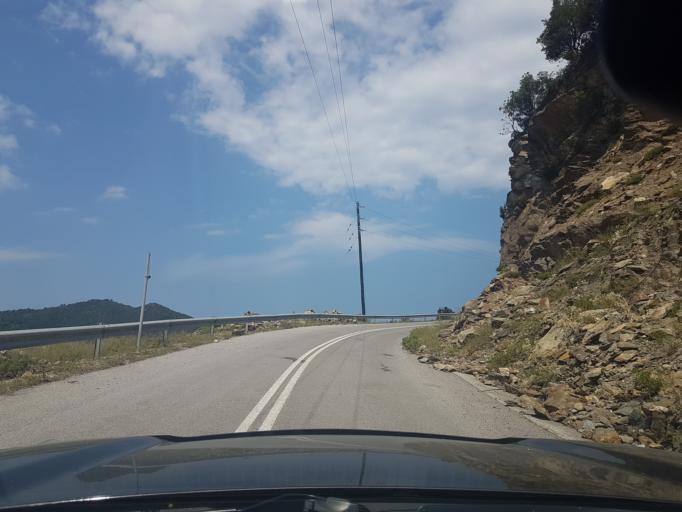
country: GR
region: Central Greece
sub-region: Nomos Evvoias
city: Kymi
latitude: 38.6339
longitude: 23.9541
